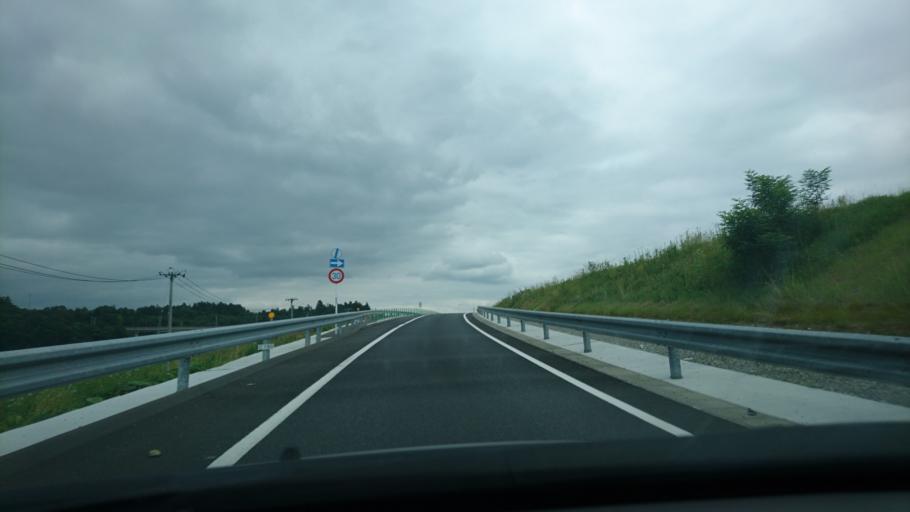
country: JP
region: Miyagi
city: Kogota
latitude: 38.7318
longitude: 141.0558
